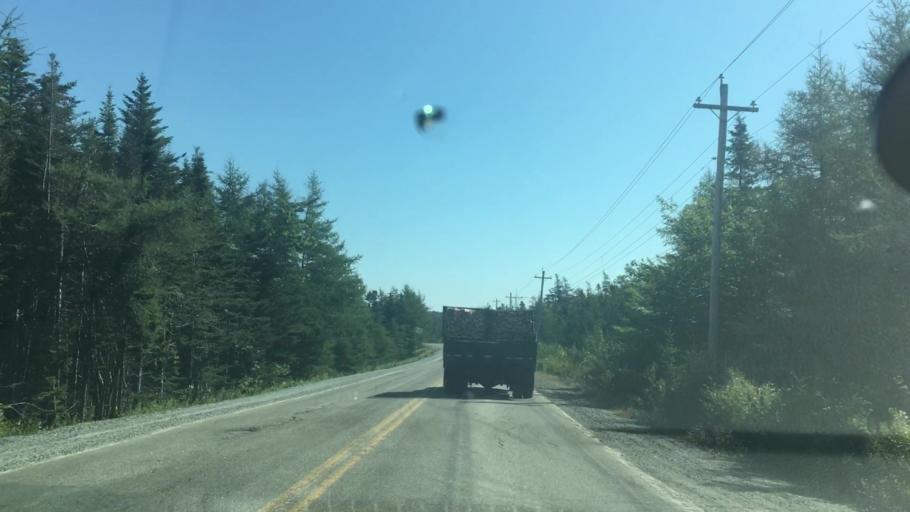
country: CA
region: Nova Scotia
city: New Glasgow
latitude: 44.9037
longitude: -62.4601
